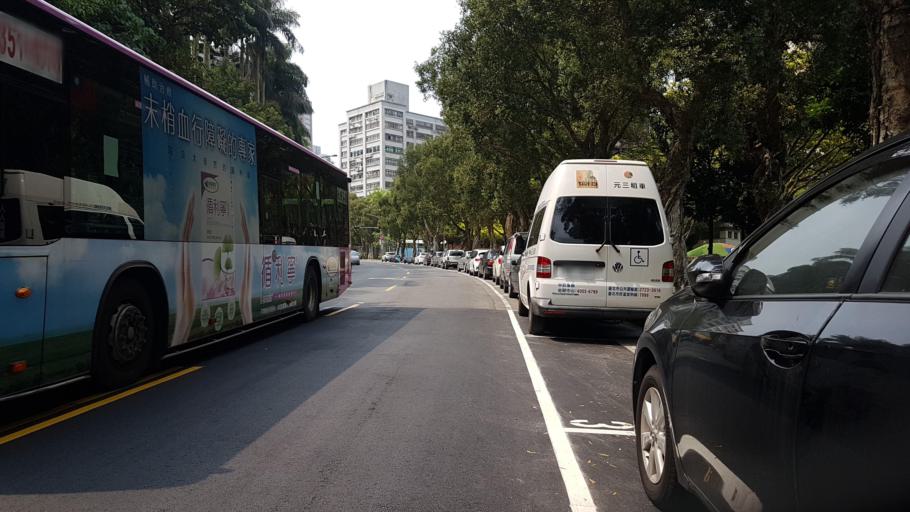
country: TW
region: Taipei
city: Taipei
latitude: 25.0006
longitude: 121.5687
